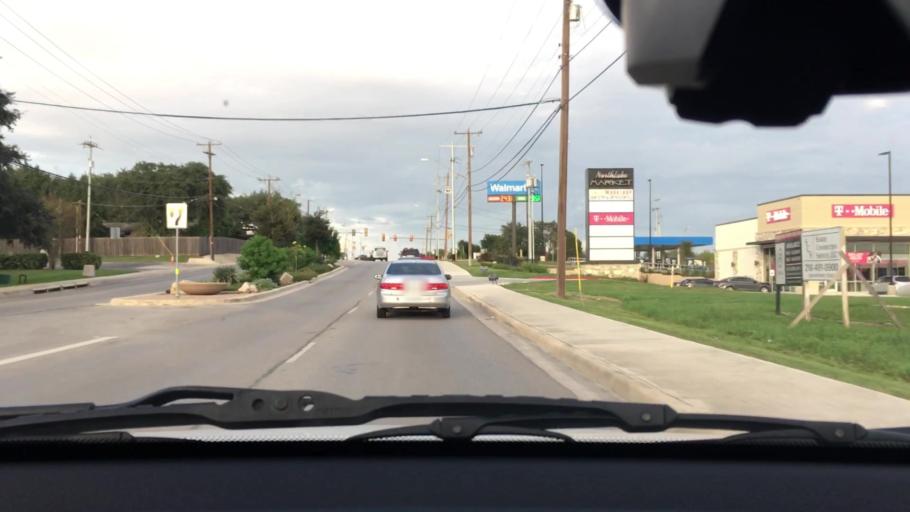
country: US
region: Texas
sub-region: Bexar County
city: Universal City
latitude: 29.5493
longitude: -98.3101
